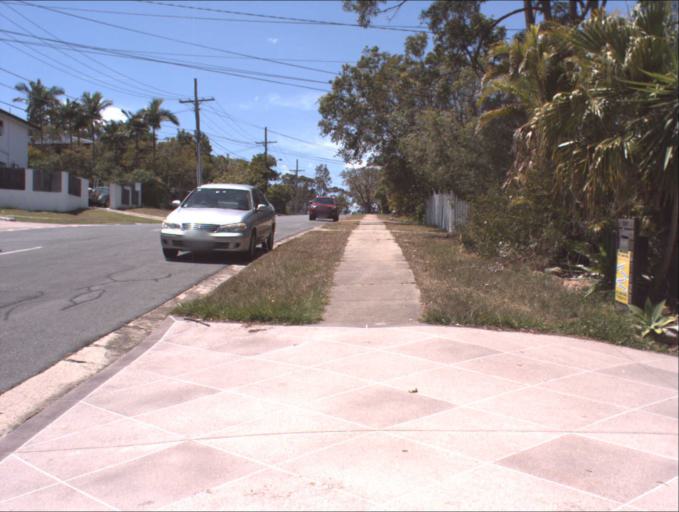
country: AU
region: Queensland
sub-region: Logan
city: Rochedale South
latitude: -27.6017
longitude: 153.1296
